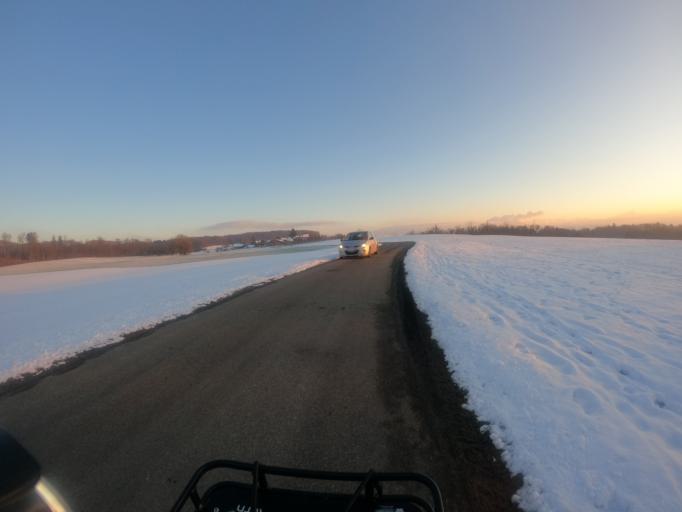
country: CH
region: Zurich
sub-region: Bezirk Affoltern
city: Affoltern / Hasenbueel
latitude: 47.2674
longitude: 8.4511
